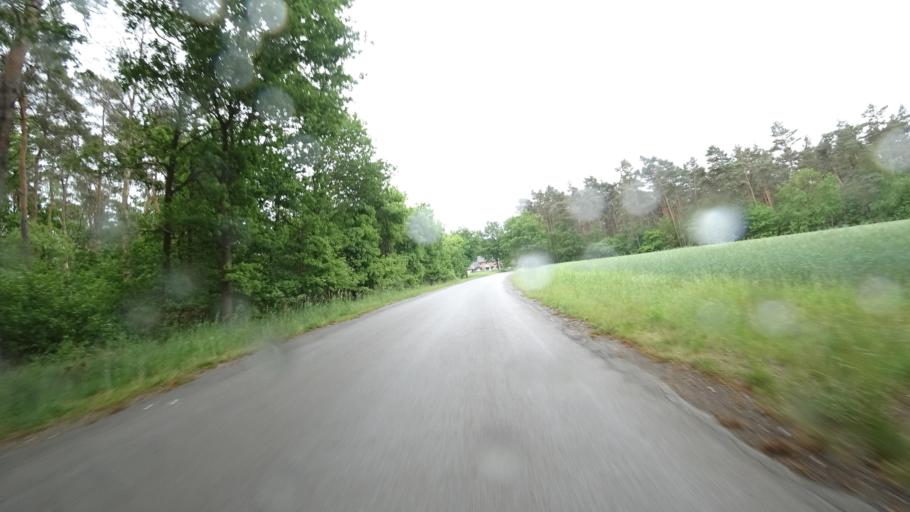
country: DE
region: North Rhine-Westphalia
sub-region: Regierungsbezirk Detmold
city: Rheda-Wiedenbruck
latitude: 51.9062
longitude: 8.2984
